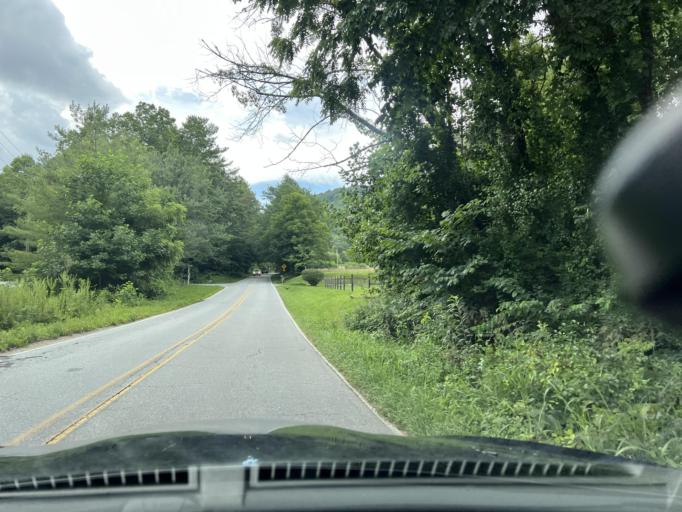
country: US
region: North Carolina
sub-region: Henderson County
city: Hoopers Creek
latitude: 35.4395
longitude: -82.4567
